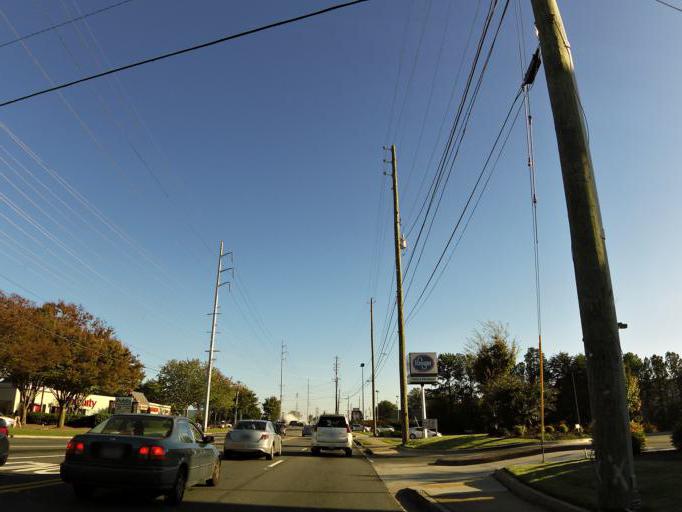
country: US
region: Georgia
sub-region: Cobb County
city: Vinings
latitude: 33.9236
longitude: -84.4687
